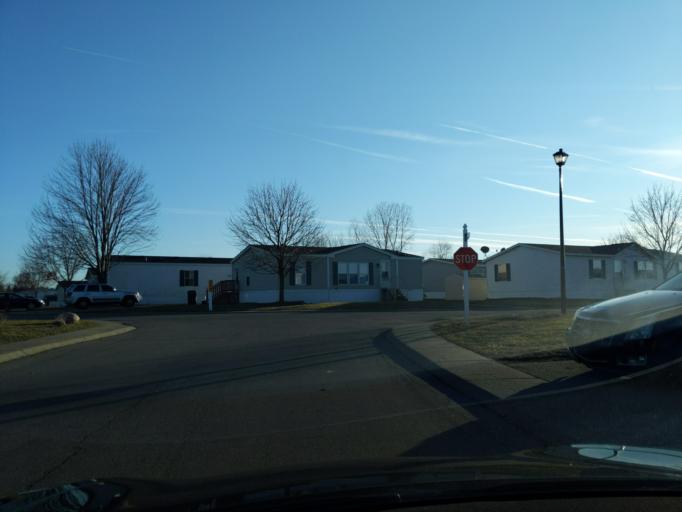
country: US
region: Michigan
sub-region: Jackson County
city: Jackson
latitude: 42.2804
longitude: -84.4729
